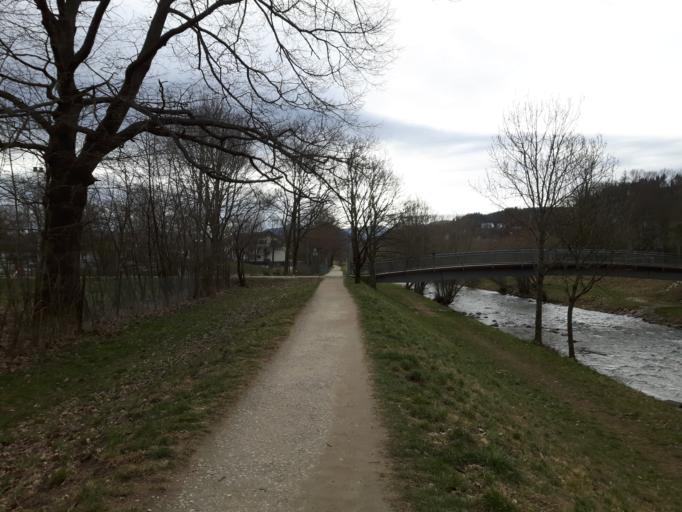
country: DE
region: Baden-Wuerttemberg
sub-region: Freiburg Region
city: Kirchzarten
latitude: 47.9843
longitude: 7.9024
